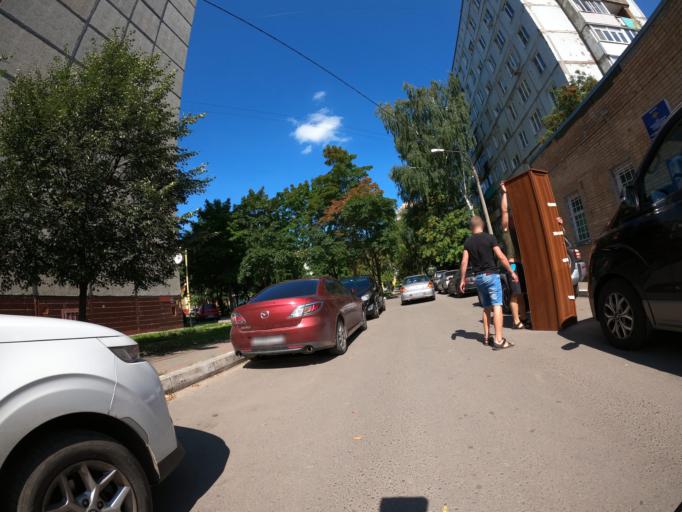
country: RU
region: Moskovskaya
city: Stupino
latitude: 54.8907
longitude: 38.0658
